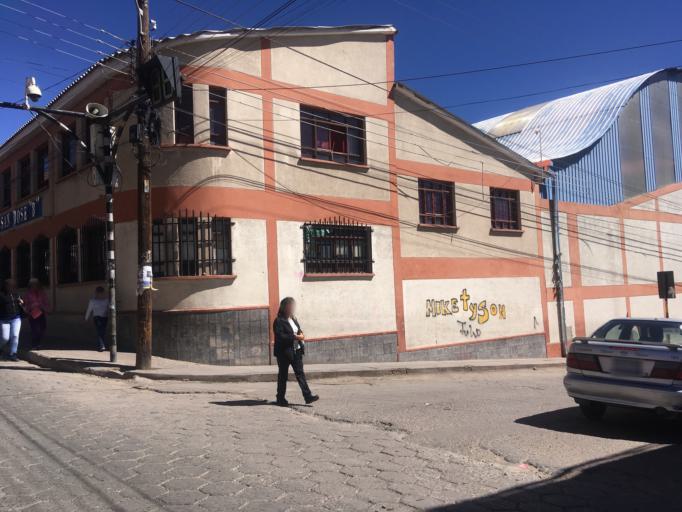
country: BO
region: Potosi
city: Potosi
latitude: -19.5811
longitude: -65.7562
